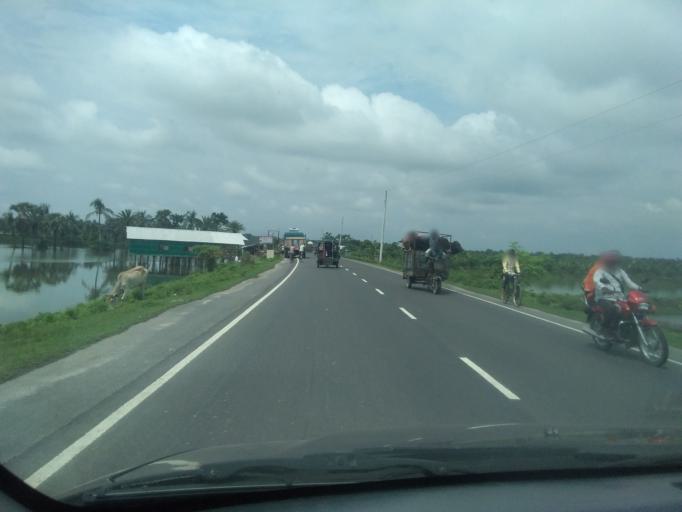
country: BD
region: Khulna
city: Kesabpur
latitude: 22.7876
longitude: 89.2152
